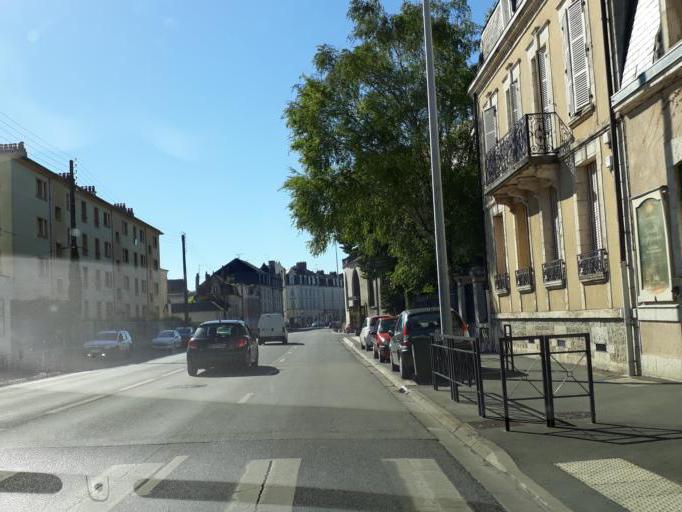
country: FR
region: Centre
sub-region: Departement du Cher
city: Bourges
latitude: 47.0855
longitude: 2.4010
